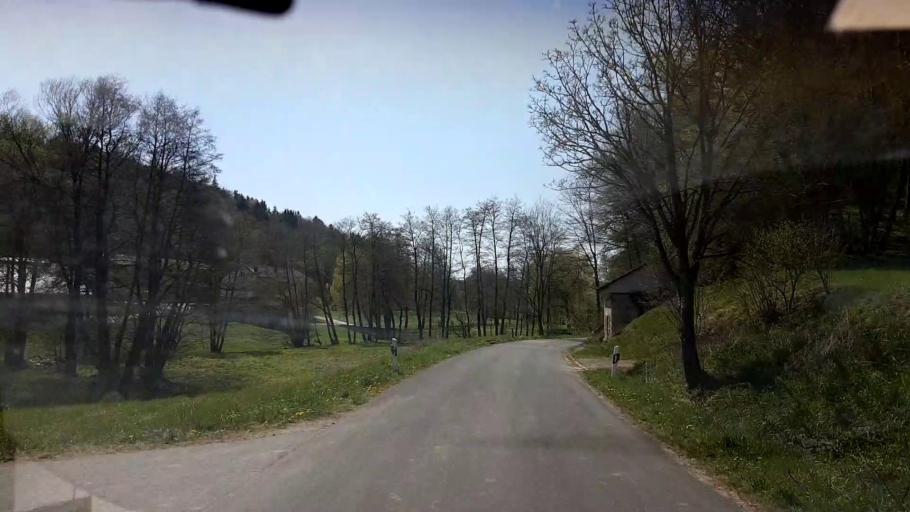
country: DE
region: Bavaria
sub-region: Upper Franconia
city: Konigsfeld
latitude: 49.9401
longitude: 11.1895
